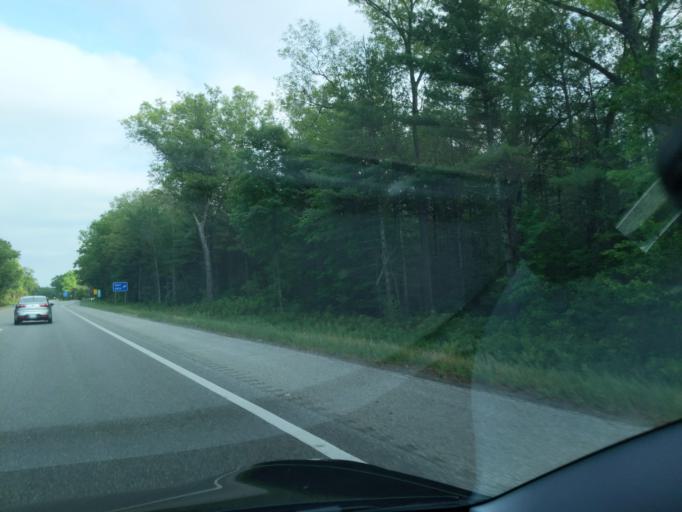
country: US
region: Michigan
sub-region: Muskegon County
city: Lakewood Club
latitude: 43.3578
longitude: -86.2594
